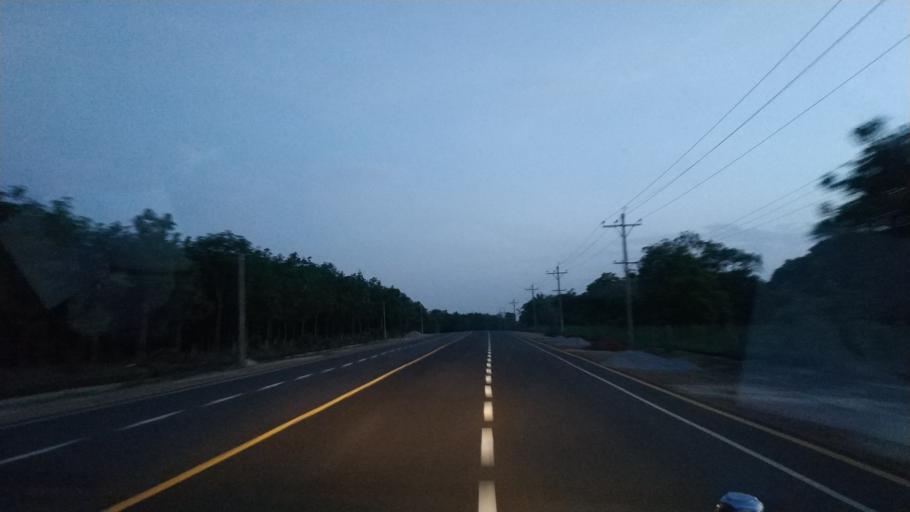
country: MM
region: Mon
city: Kyaikto
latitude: 17.3753
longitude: 97.0524
